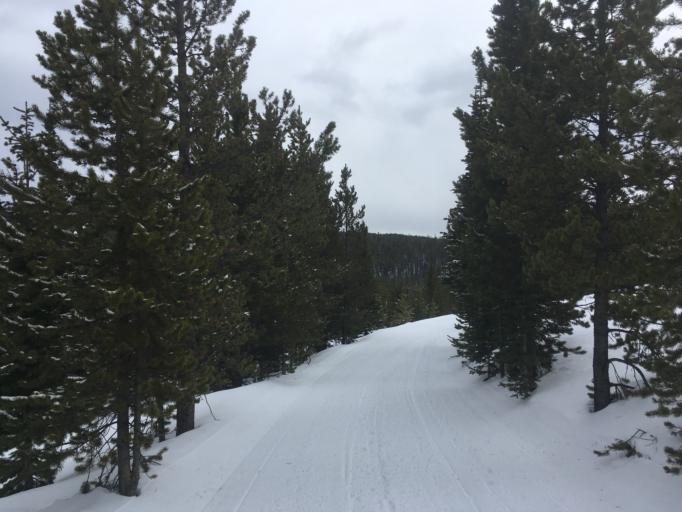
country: US
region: Montana
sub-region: Meagher County
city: White Sulphur Springs
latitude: 46.8480
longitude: -110.7076
